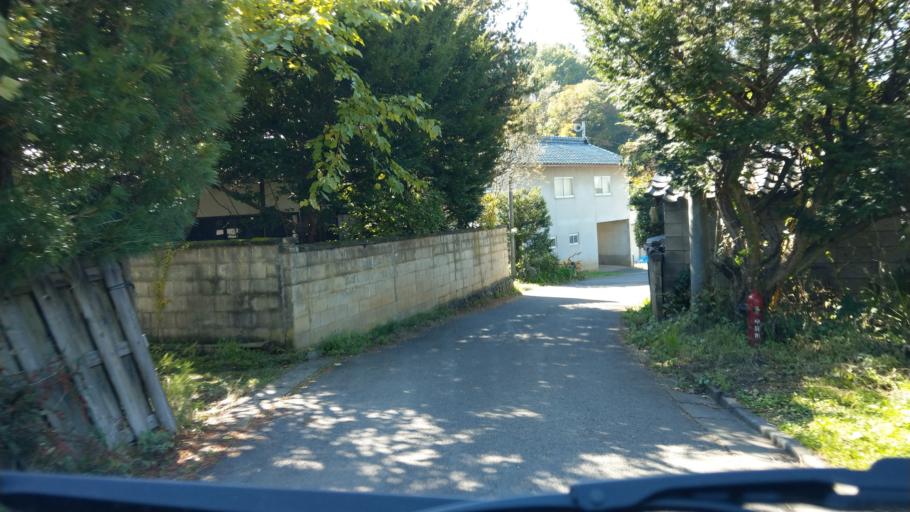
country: JP
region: Nagano
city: Komoro
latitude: 36.3648
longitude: 138.4028
